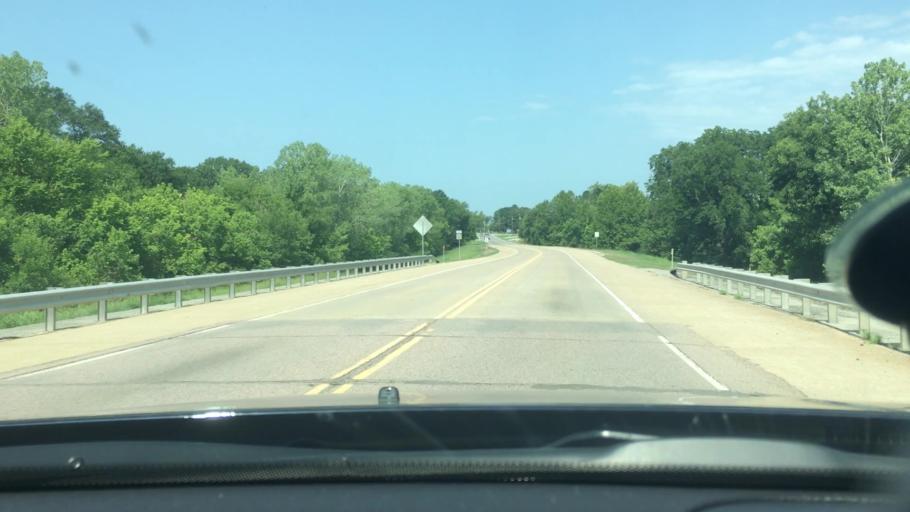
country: US
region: Oklahoma
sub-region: Atoka County
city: Atoka
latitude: 34.3935
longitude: -96.1281
